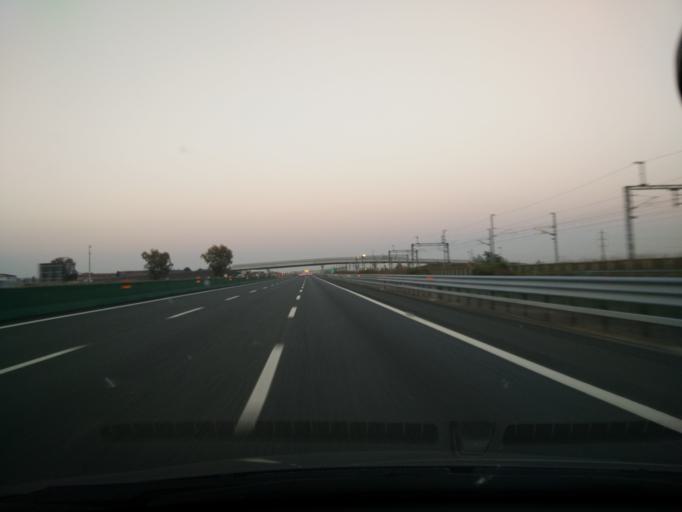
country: IT
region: Piedmont
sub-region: Provincia di Vercelli
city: Alice Castello
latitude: 45.3401
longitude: 8.0933
